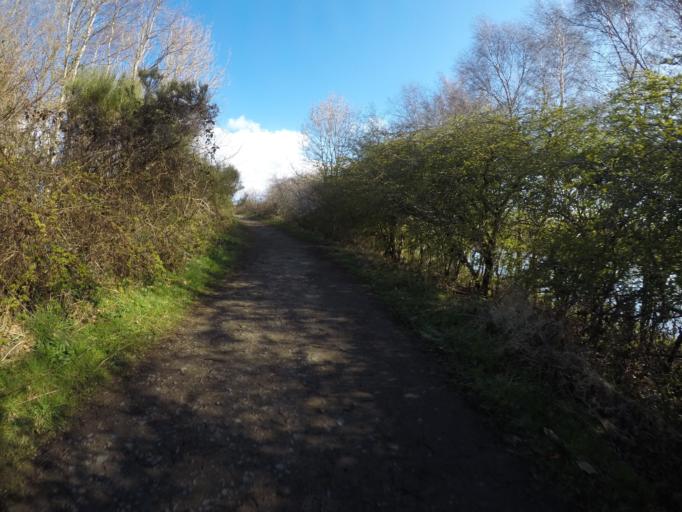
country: GB
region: Scotland
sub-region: North Ayrshire
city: Irvine
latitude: 55.6448
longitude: -4.6624
